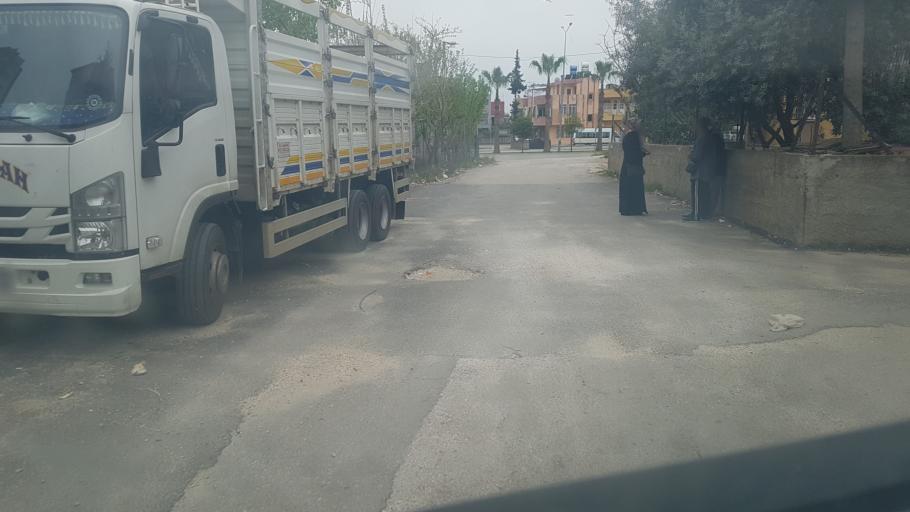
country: TR
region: Adana
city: Seyhan
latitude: 37.0217
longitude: 35.2736
